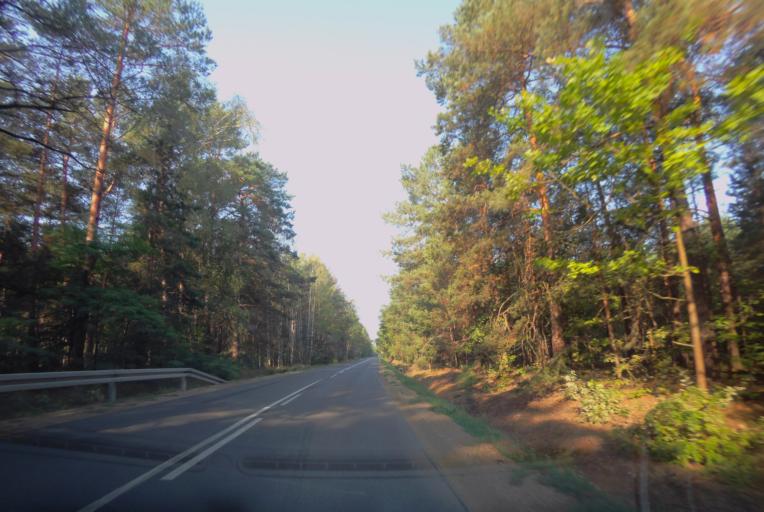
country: PL
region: Subcarpathian Voivodeship
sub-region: Powiat nizanski
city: Jarocin
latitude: 50.5101
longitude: 22.3312
